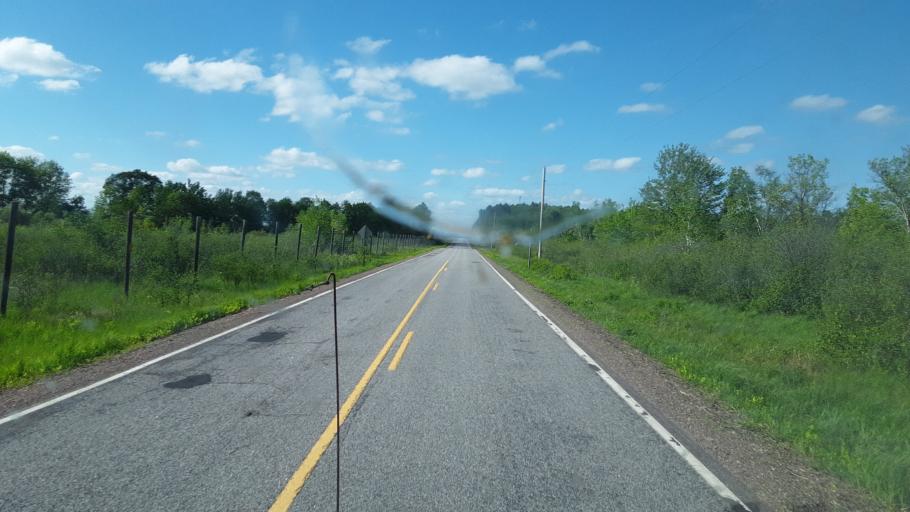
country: US
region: Wisconsin
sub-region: Wood County
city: Nekoosa
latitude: 44.3248
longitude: -90.1307
